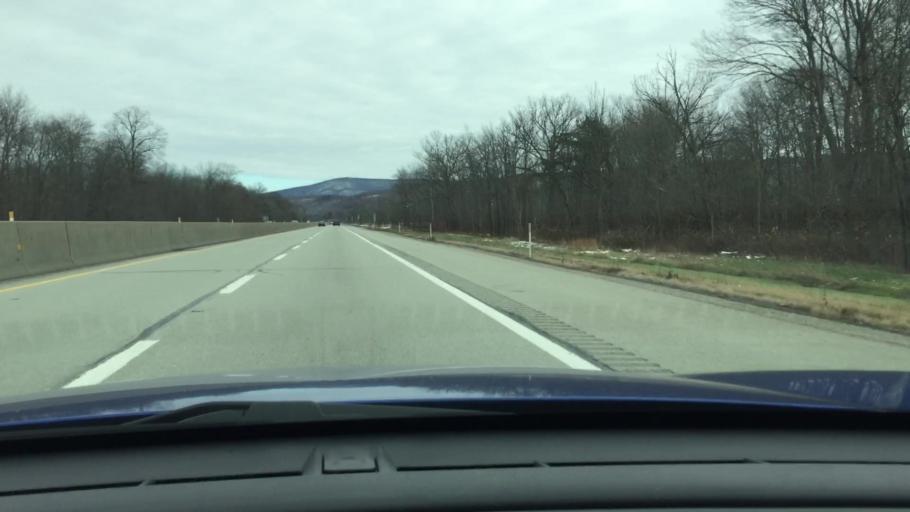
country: US
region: Pennsylvania
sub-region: Bedford County
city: Bedford
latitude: 40.0104
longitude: -78.6676
